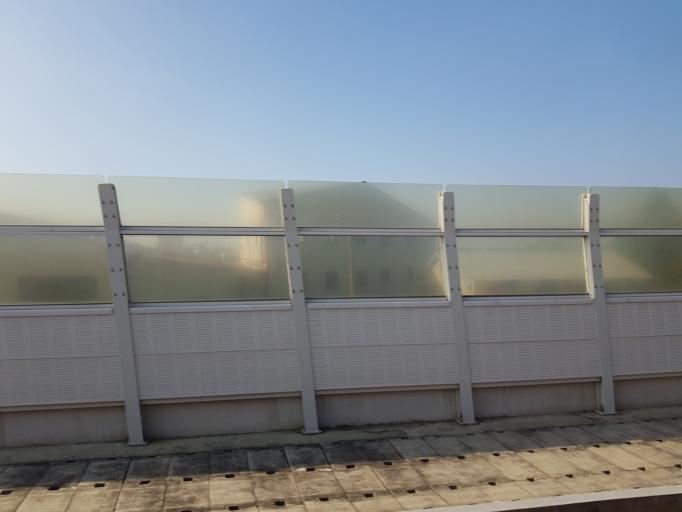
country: TW
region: Taiwan
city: Fengyuan
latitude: 24.2595
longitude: 120.7278
